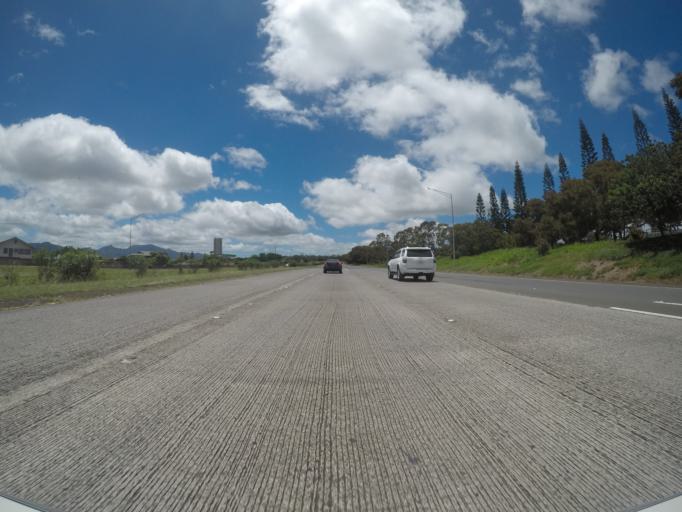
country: US
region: Hawaii
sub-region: Honolulu County
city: Waipi'o Acres
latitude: 21.4685
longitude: -158.0066
